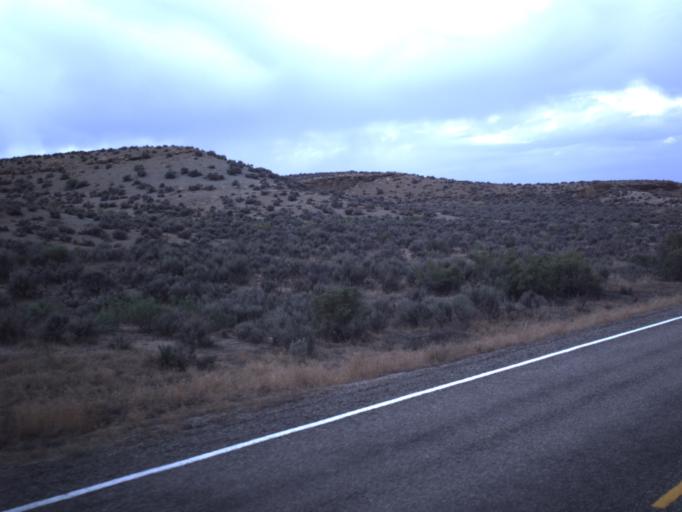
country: US
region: Colorado
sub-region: Rio Blanco County
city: Rangely
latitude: 40.0403
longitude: -109.1855
